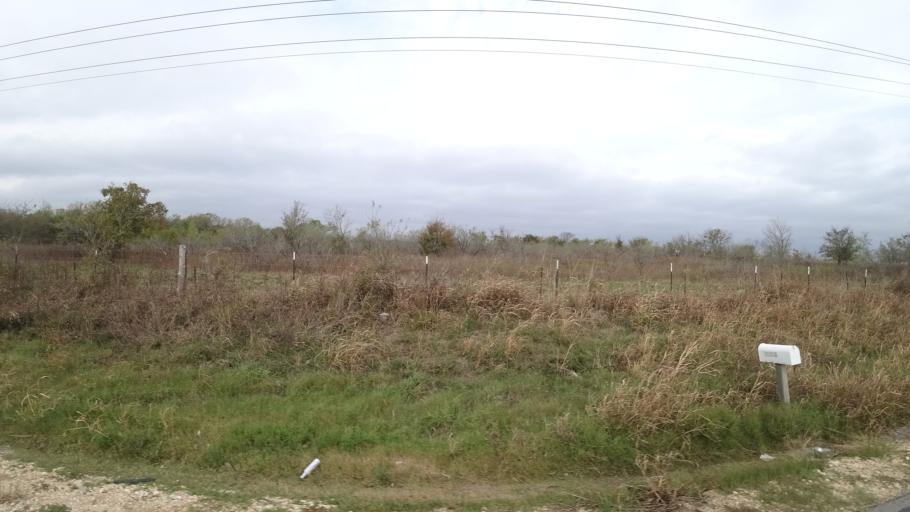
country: US
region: Texas
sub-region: Travis County
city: Manor
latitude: 30.3750
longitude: -97.5615
